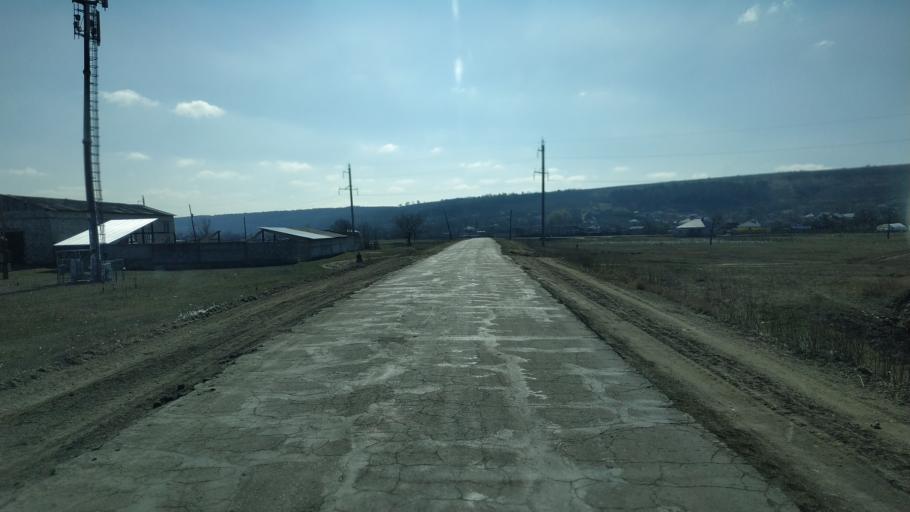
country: MD
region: Hincesti
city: Hincesti
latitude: 46.7529
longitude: 28.6521
